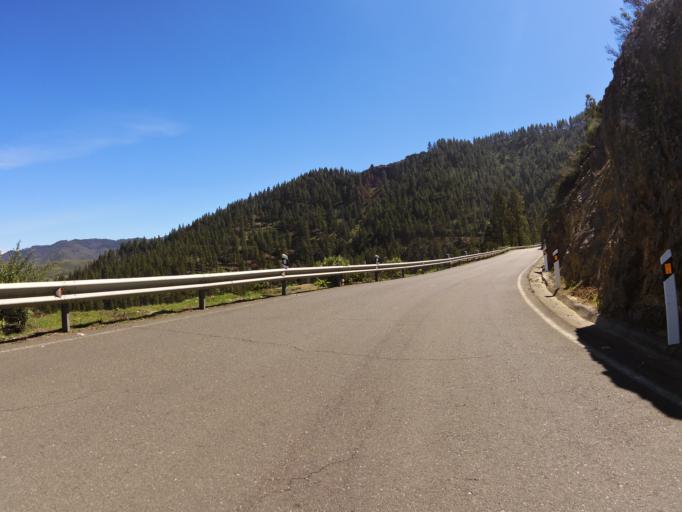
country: ES
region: Canary Islands
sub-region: Provincia de Las Palmas
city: Artenara
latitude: 28.0282
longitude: -15.6655
